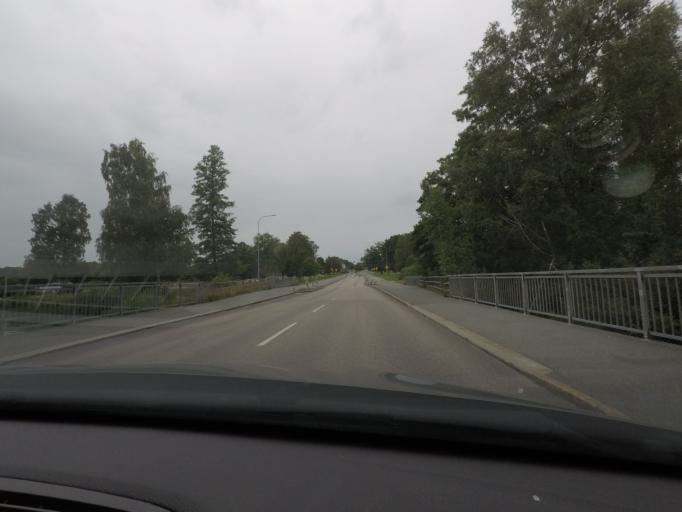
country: SE
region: Skane
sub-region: Osby Kommun
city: Osby
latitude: 56.3782
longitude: 14.0032
